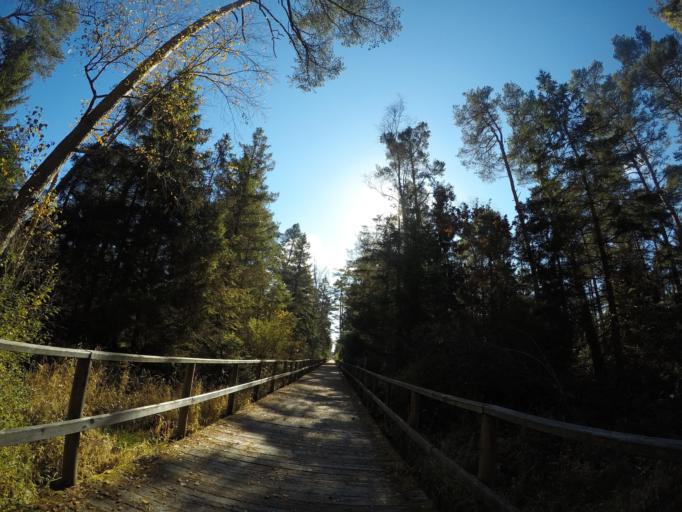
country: DE
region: Baden-Wuerttemberg
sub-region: Tuebingen Region
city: Bad Buchau
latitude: 48.0792
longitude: 9.6015
